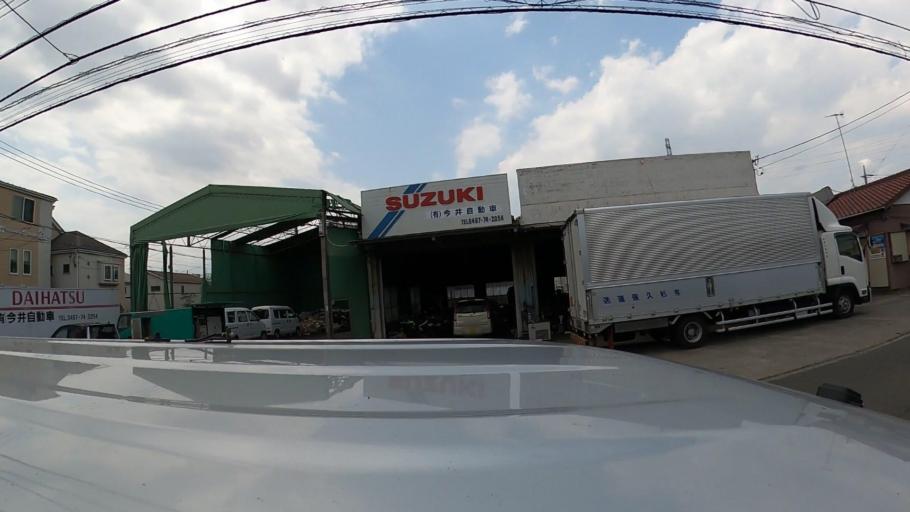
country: JP
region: Kanagawa
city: Chigasaki
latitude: 35.3710
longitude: 139.3902
